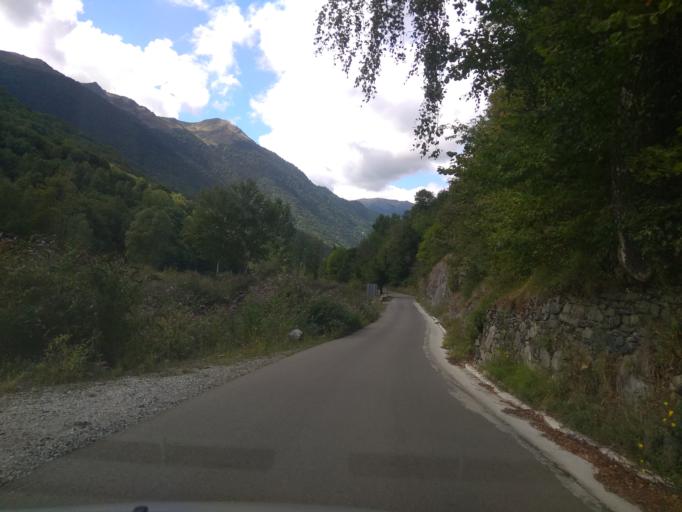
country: ES
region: Catalonia
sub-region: Provincia de Lleida
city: Vielha
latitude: 42.7325
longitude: 0.7229
